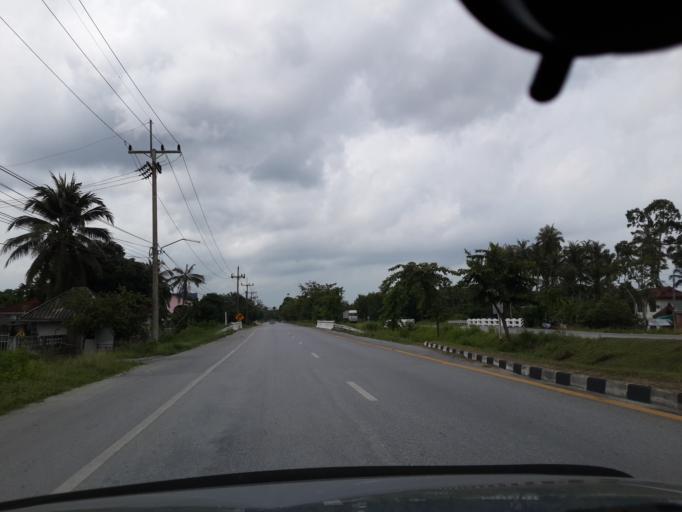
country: TH
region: Pattani
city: Yaring
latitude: 6.8676
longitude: 101.3303
